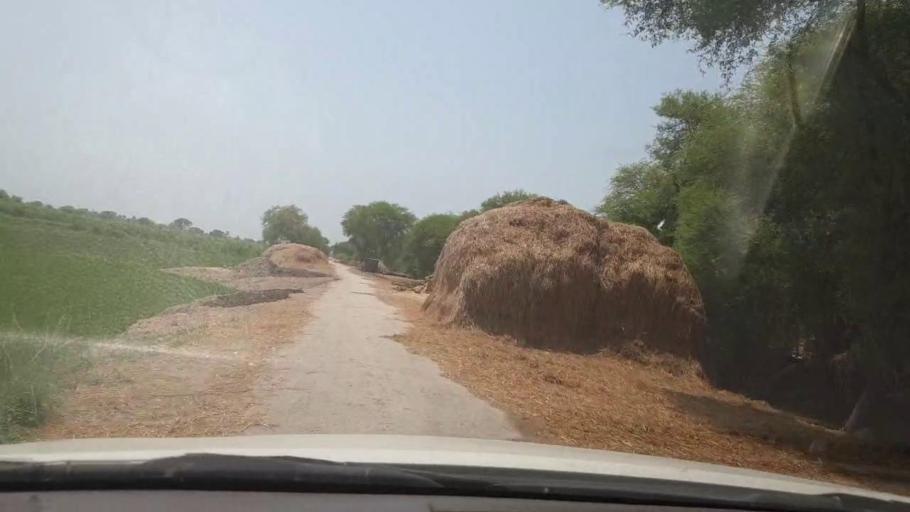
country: PK
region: Sindh
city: Shikarpur
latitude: 28.0756
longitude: 68.5452
